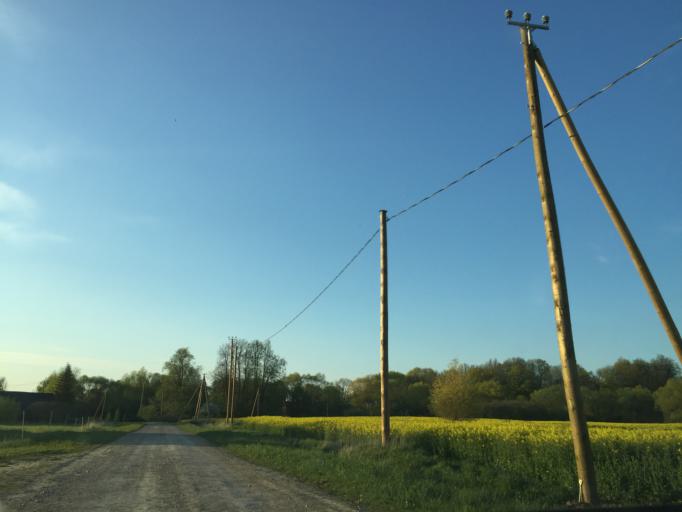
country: LV
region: Bauskas Rajons
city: Bauska
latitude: 56.3157
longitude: 24.1795
